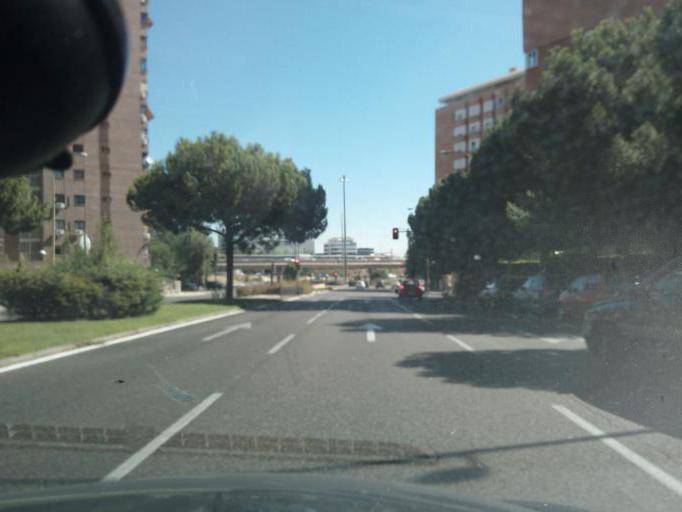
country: ES
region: Madrid
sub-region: Provincia de Madrid
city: Pinar de Chamartin
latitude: 40.4822
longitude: -3.6649
